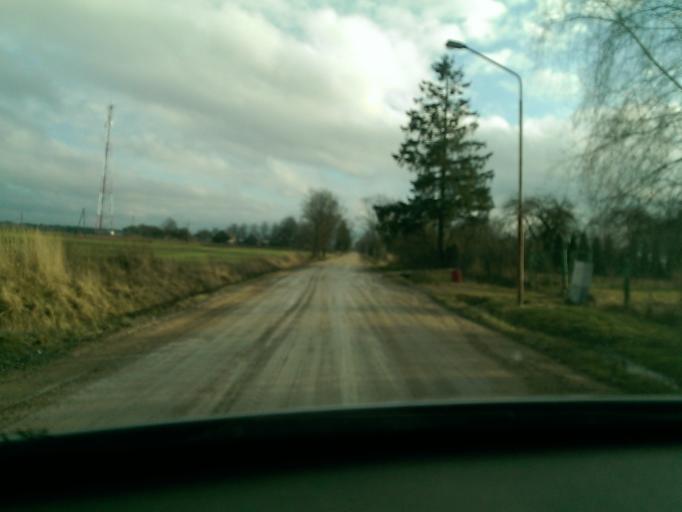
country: LV
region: Kuldigas Rajons
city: Kuldiga
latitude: 56.9769
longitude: 21.9874
